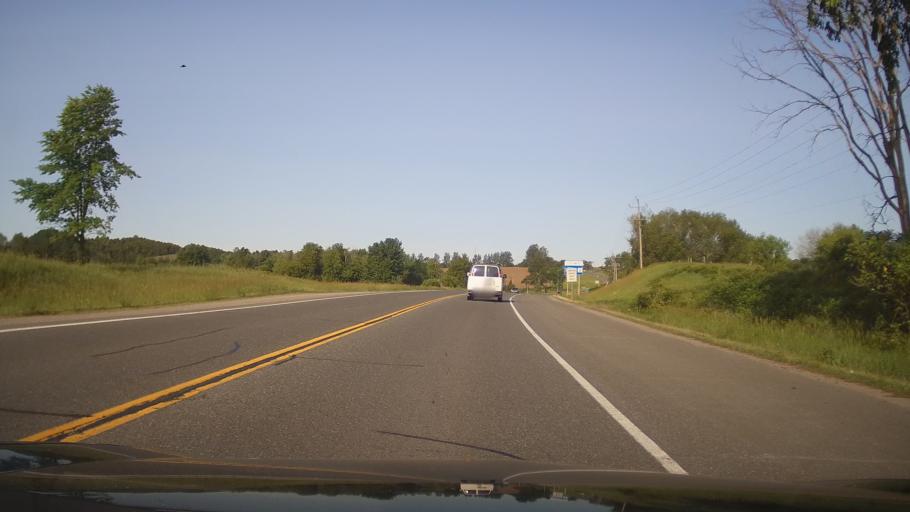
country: CA
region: Ontario
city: Peterborough
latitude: 44.3655
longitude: -78.0017
